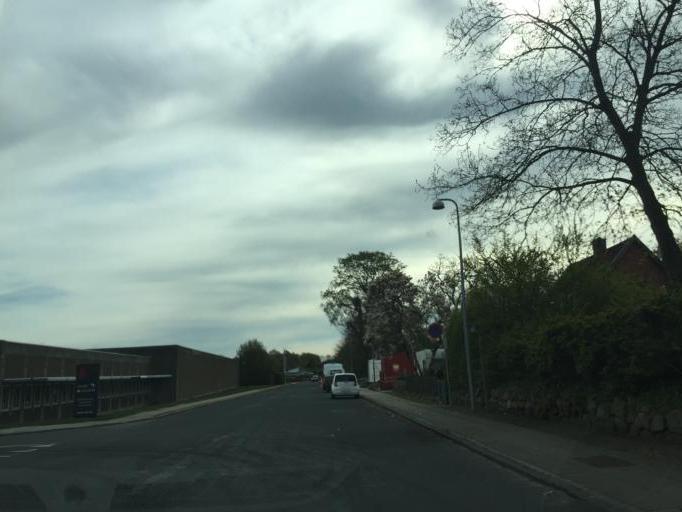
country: DK
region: South Denmark
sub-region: Odense Kommune
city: Odense
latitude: 55.4132
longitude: 10.3424
